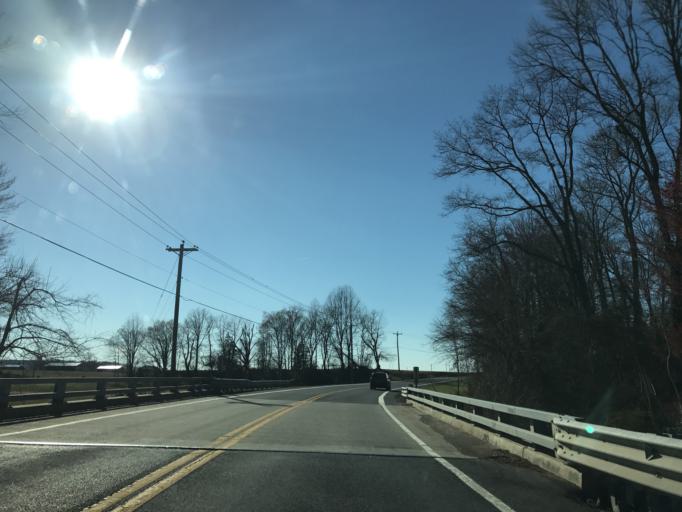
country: US
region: Maryland
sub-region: Caroline County
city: Ridgely
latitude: 39.0092
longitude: -75.9369
